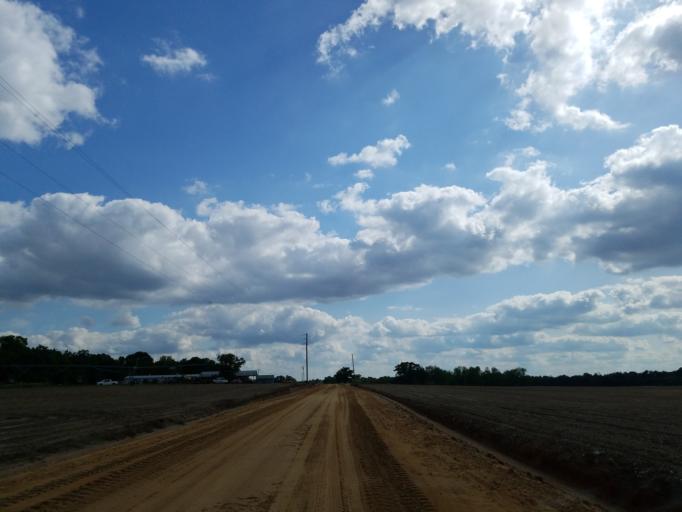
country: US
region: Georgia
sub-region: Dooly County
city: Unadilla
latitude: 32.2319
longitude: -83.7631
